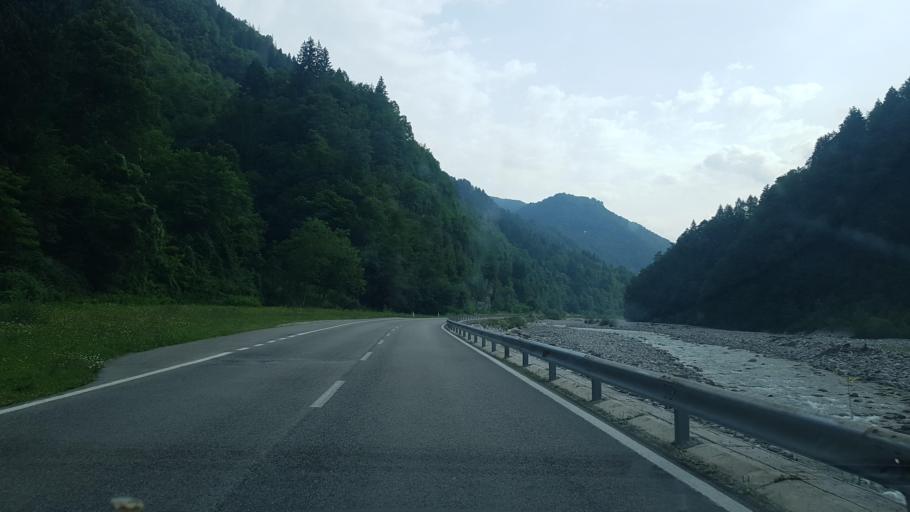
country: IT
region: Friuli Venezia Giulia
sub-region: Provincia di Udine
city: Zuglio
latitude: 46.4612
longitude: 13.0446
